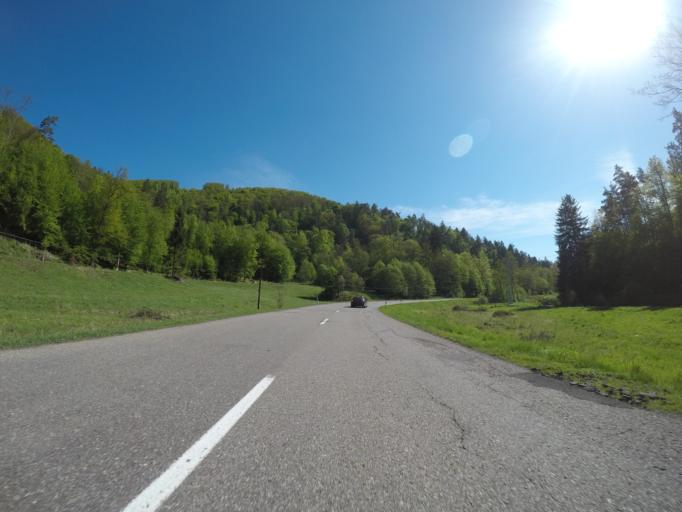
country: SK
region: Banskobystricky
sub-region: Okres Banska Bystrica
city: Banska Stiavnica
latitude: 48.5090
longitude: 18.9756
